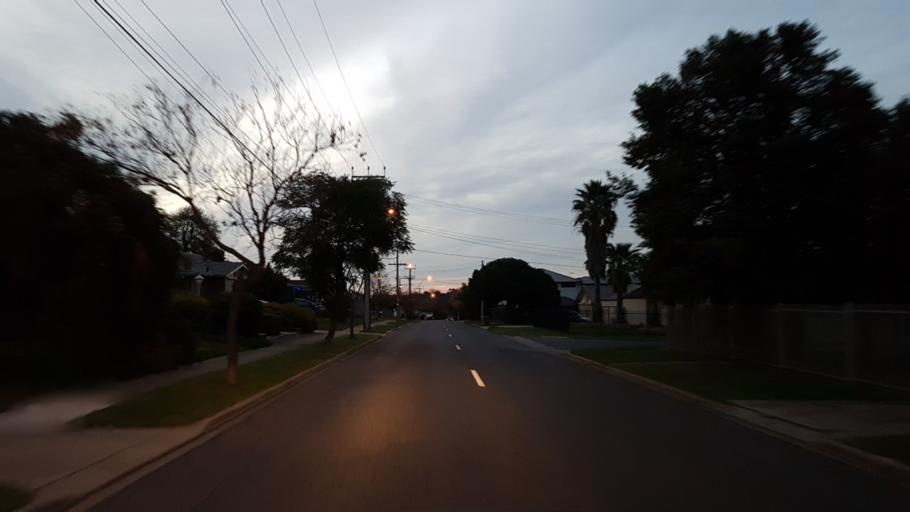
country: AU
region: South Australia
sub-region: Port Adelaide Enfield
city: Gilles Plains
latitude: -34.8507
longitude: 138.6654
